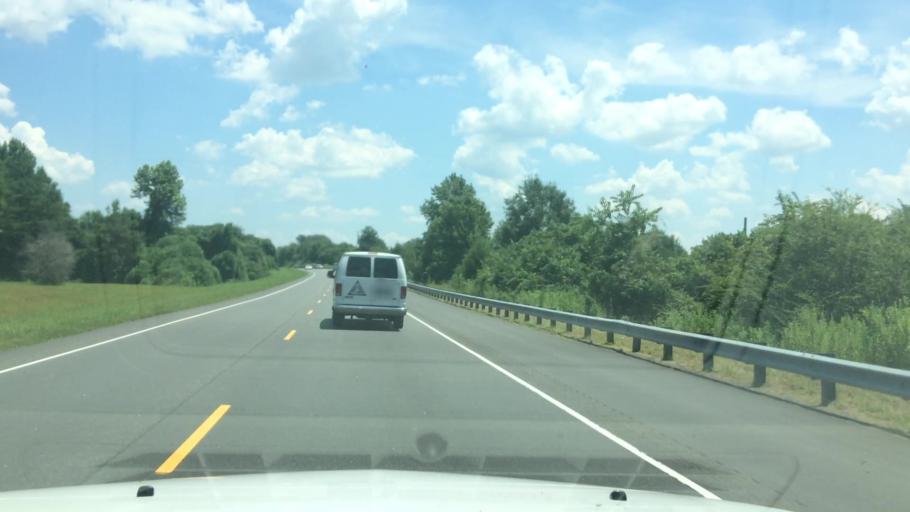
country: US
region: North Carolina
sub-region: Iredell County
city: Statesville
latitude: 35.8059
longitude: -80.9659
